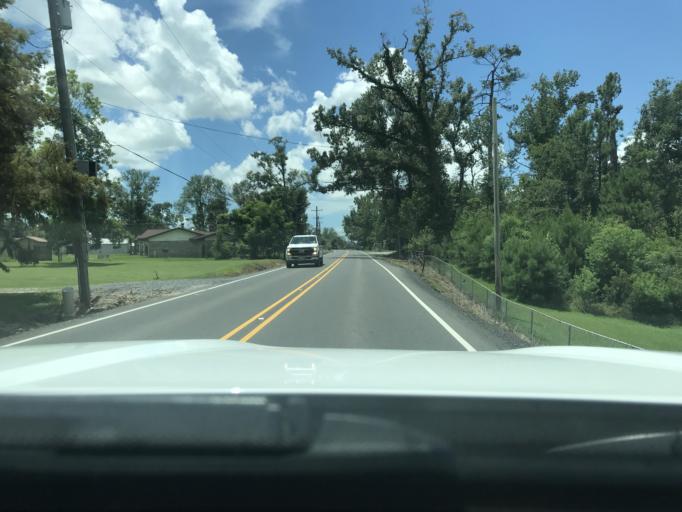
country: US
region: Louisiana
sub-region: Calcasieu Parish
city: Moss Bluff
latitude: 30.3037
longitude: -93.1810
